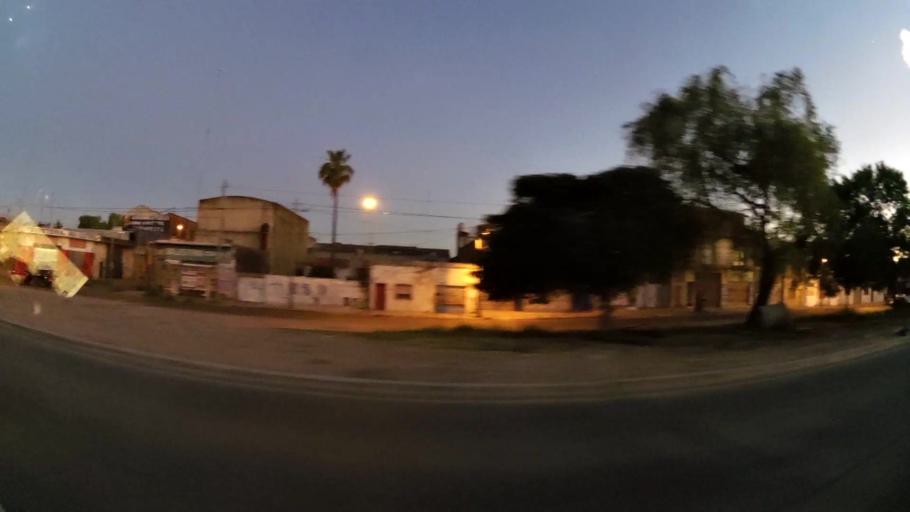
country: AR
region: Buenos Aires
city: San Justo
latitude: -34.7105
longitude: -58.5888
